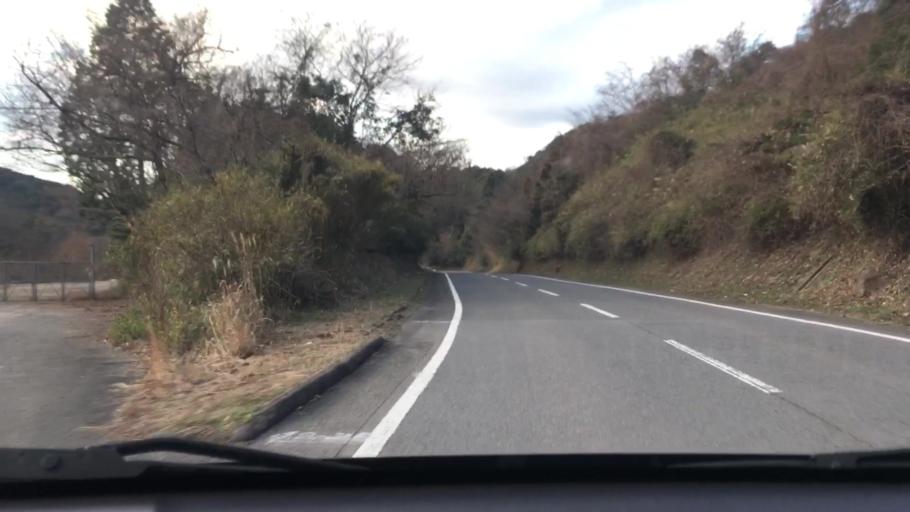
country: JP
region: Oita
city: Hiji
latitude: 33.4115
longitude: 131.4249
